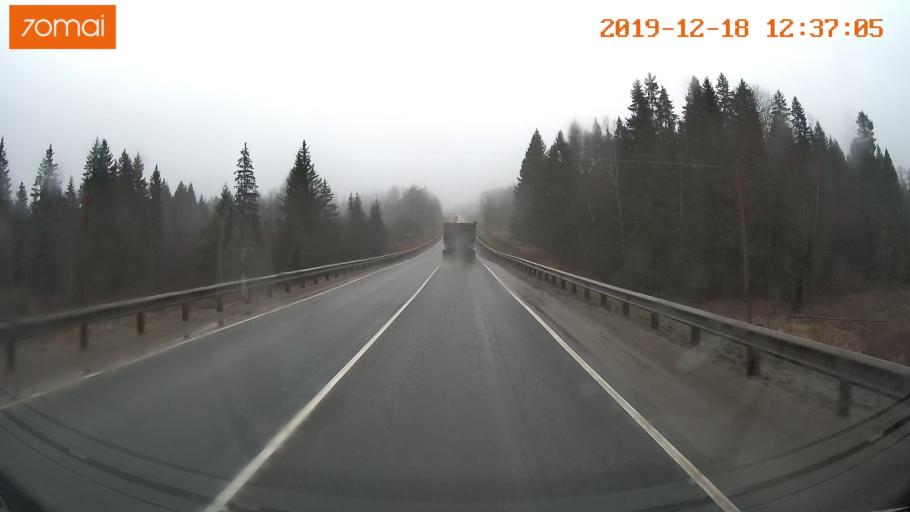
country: RU
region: Moskovskaya
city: Rumyantsevo
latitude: 56.1420
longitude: 36.5989
